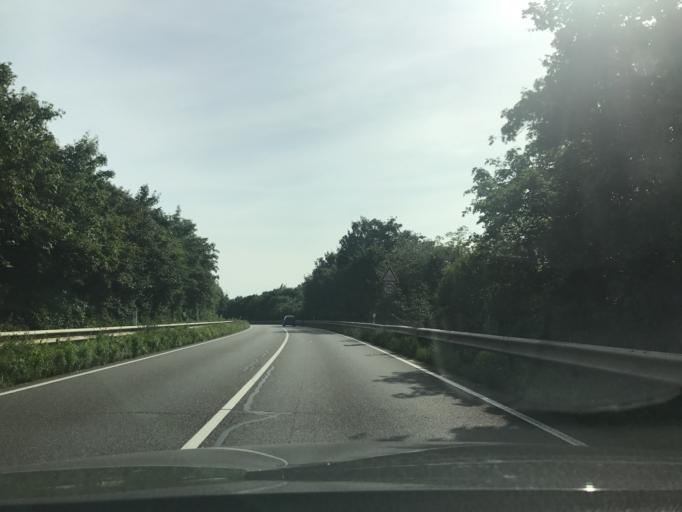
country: DE
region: North Rhine-Westphalia
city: Kempen
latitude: 51.3872
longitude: 6.4168
